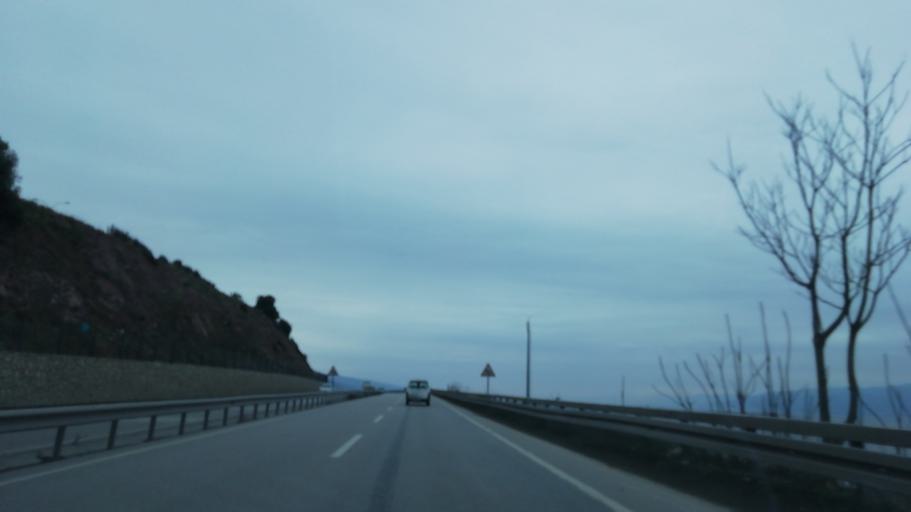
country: TR
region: Kocaeli
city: Tavsancil
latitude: 40.7682
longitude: 29.5742
